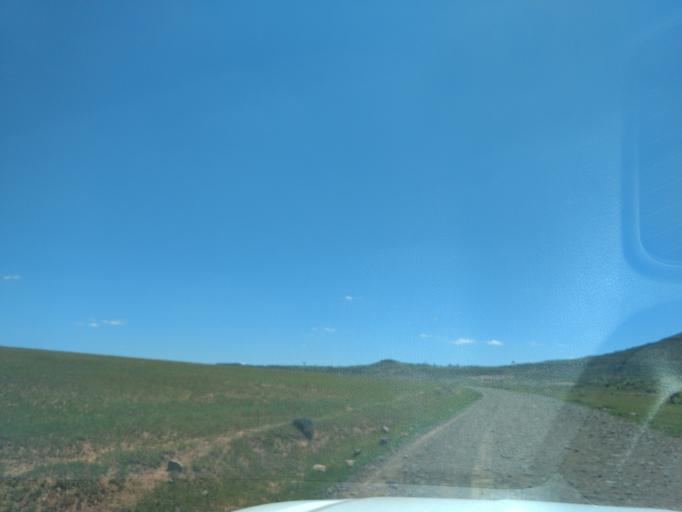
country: LS
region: Maseru
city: Maseru
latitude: -29.4768
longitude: 27.3746
